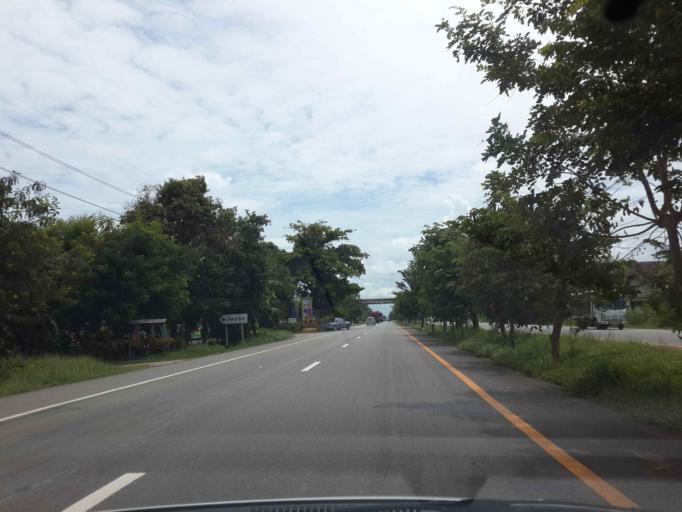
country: TH
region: Ratchaburi
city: Pak Tho
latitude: 13.4139
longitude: 99.8109
